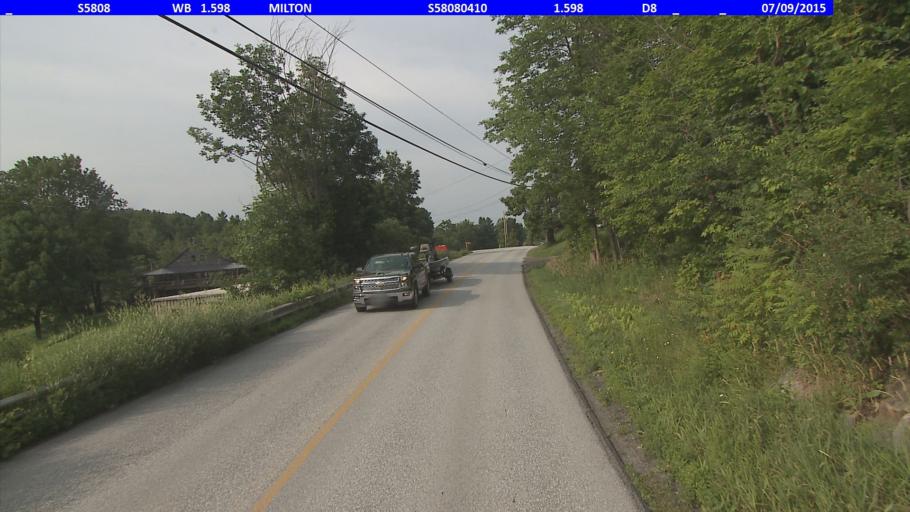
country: US
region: Vermont
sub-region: Chittenden County
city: Milton
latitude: 44.6380
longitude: -73.0837
